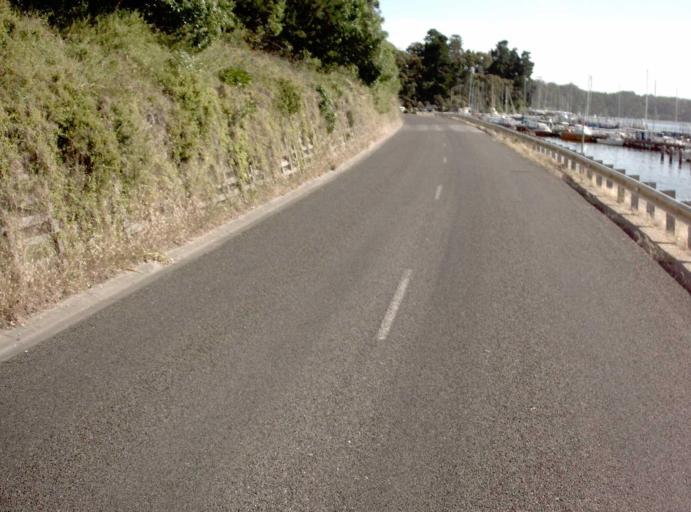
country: AU
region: Victoria
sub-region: East Gippsland
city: Lakes Entrance
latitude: -37.8894
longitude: 147.8561
